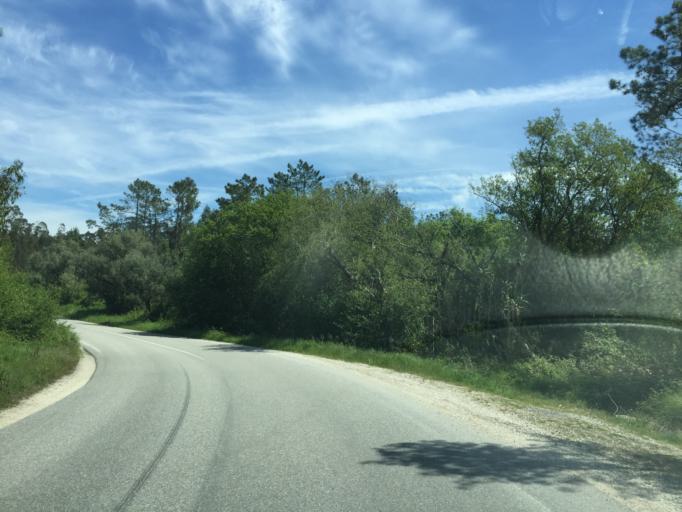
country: PT
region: Coimbra
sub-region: Soure
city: Soure
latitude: 40.0553
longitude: -8.6625
